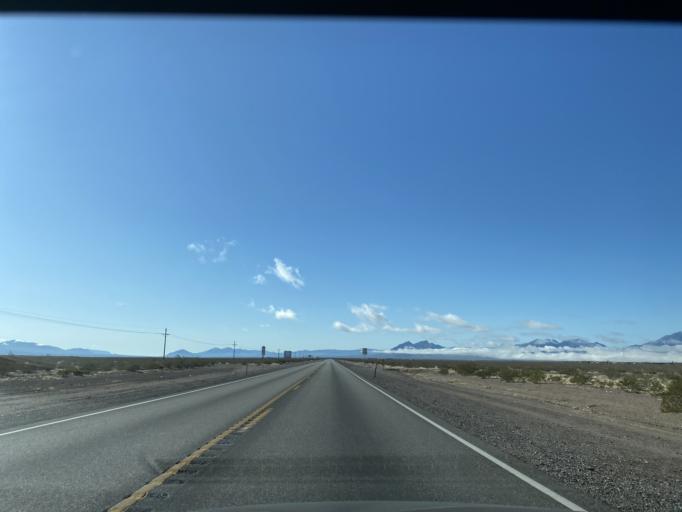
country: US
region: Nevada
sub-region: Nye County
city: Beatty
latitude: 36.5686
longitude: -116.4137
